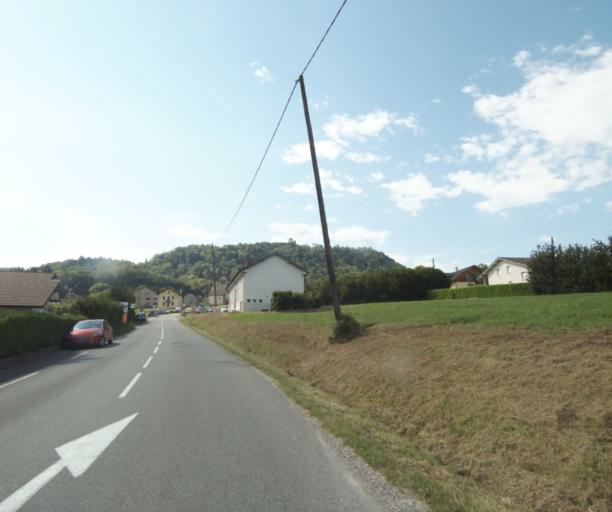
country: FR
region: Rhone-Alpes
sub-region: Departement de la Haute-Savoie
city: Allinges
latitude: 46.3386
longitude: 6.4630
